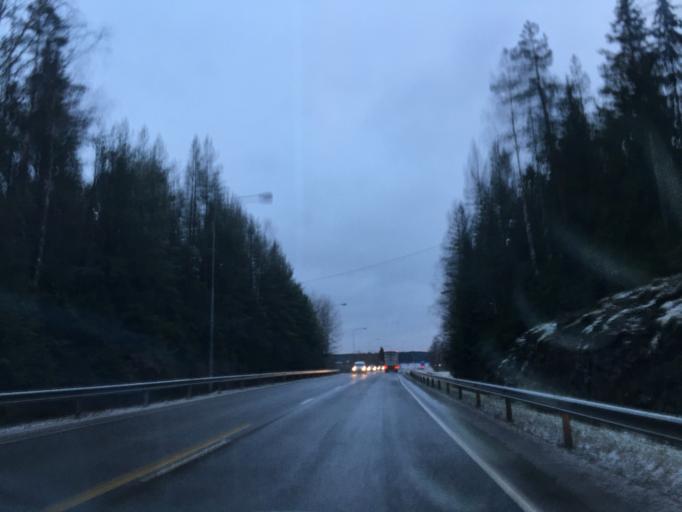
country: FI
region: Varsinais-Suomi
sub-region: Loimaa
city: Aura
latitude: 60.6500
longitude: 22.5690
